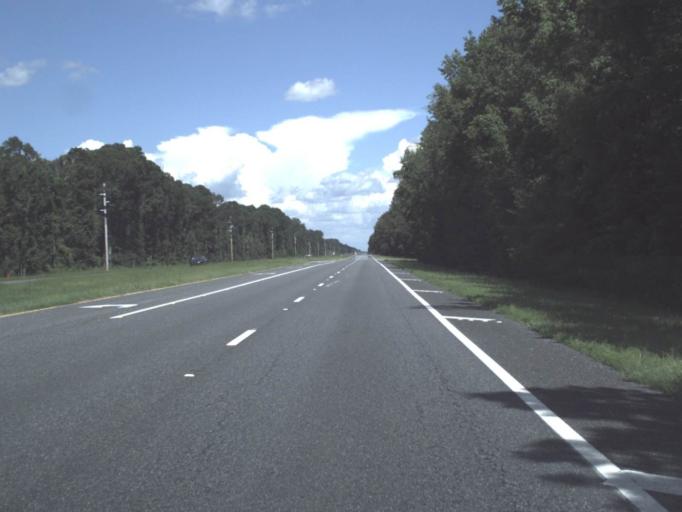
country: US
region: Florida
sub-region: Dixie County
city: Cross City
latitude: 29.6784
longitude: -83.2532
